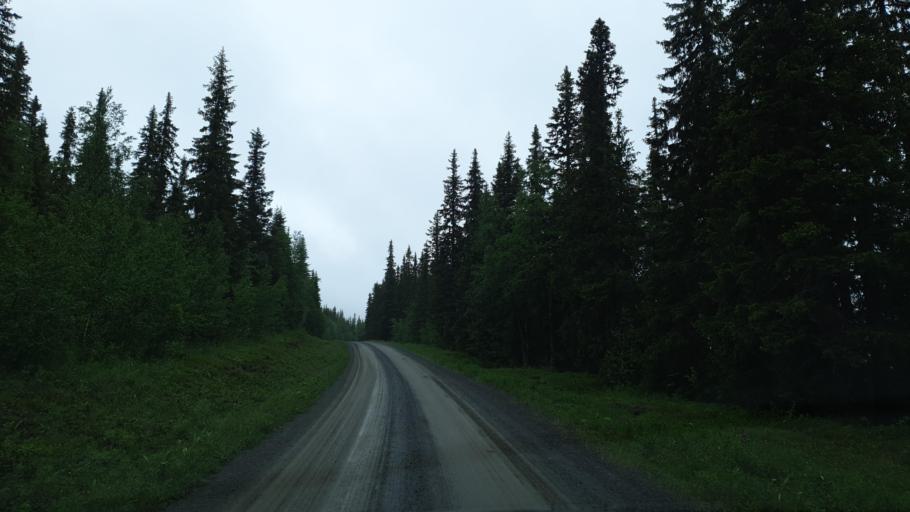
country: SE
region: Vaesterbotten
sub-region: Vilhelmina Kommun
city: Sjoberg
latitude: 65.3307
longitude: 15.9093
